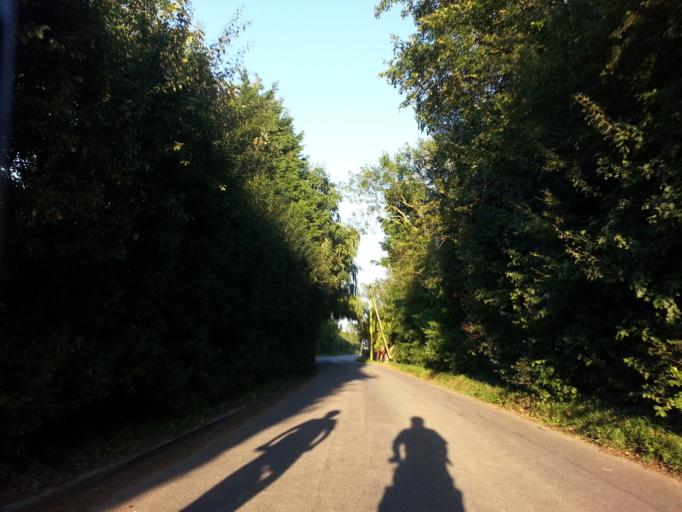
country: GB
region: England
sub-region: Suffolk
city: Kesgrave
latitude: 52.1228
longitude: 1.2270
